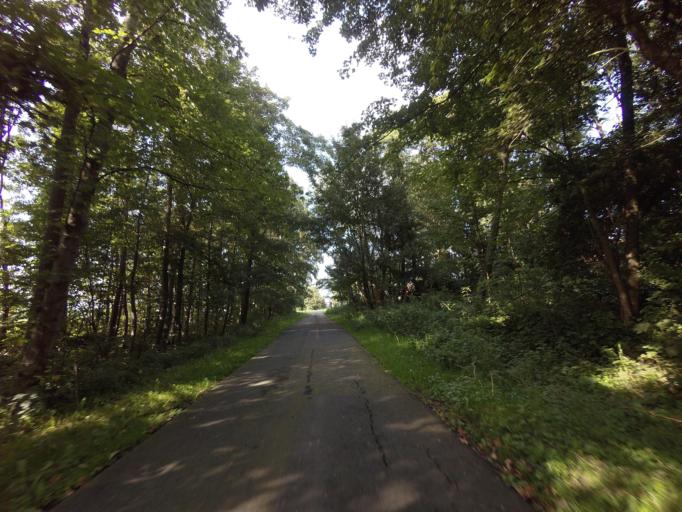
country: NL
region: Flevoland
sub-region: Gemeente Noordoostpolder
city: Ens
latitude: 52.6523
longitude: 5.7748
